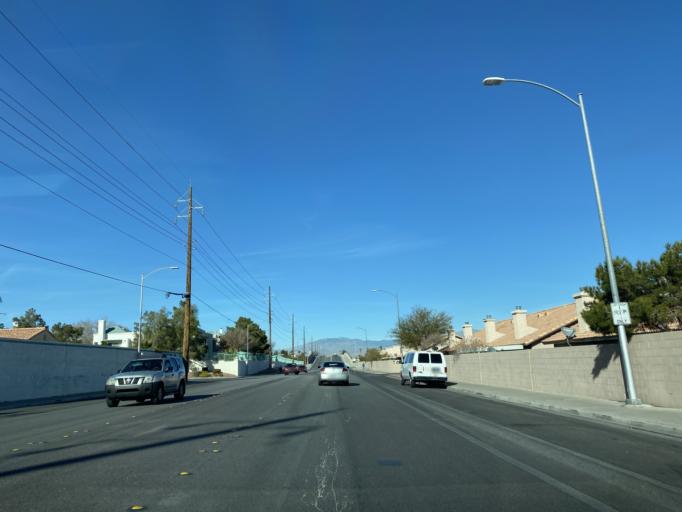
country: US
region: Nevada
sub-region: Clark County
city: Spring Valley
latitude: 36.1751
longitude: -115.2508
